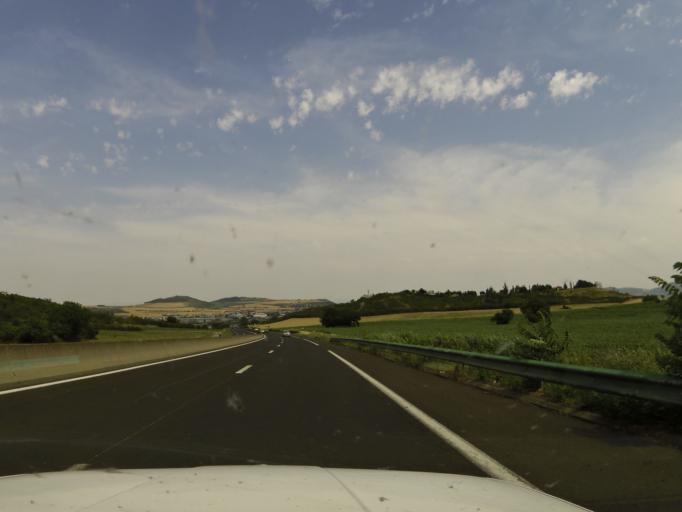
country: FR
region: Auvergne
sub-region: Departement du Puy-de-Dome
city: Perignat-les-Sarlieve
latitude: 45.7400
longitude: 3.1249
